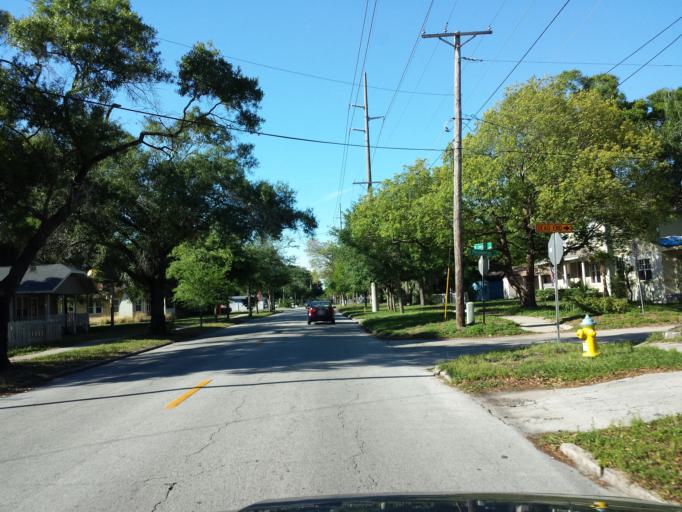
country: US
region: Florida
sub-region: Hillsborough County
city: Egypt Lake-Leto
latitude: 28.0091
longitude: -82.4554
